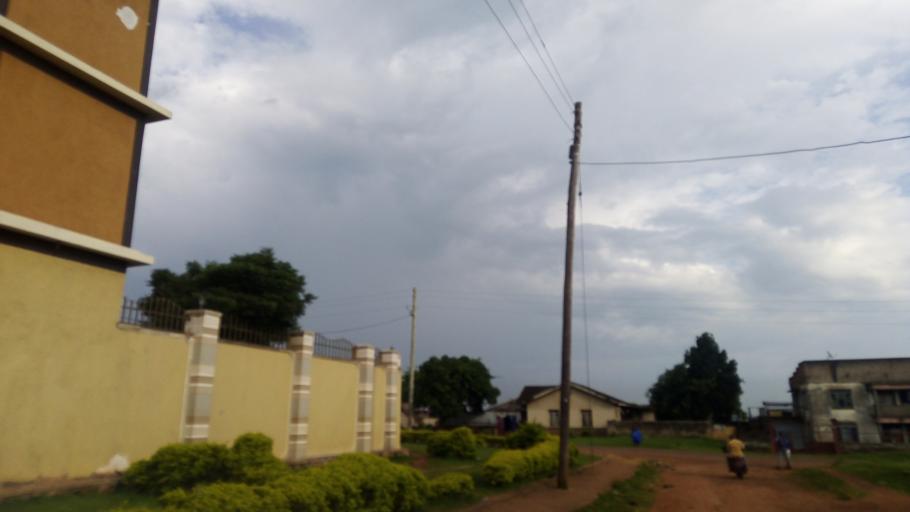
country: UG
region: Eastern Region
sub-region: Mbale District
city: Mbale
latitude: 1.0775
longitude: 34.1668
